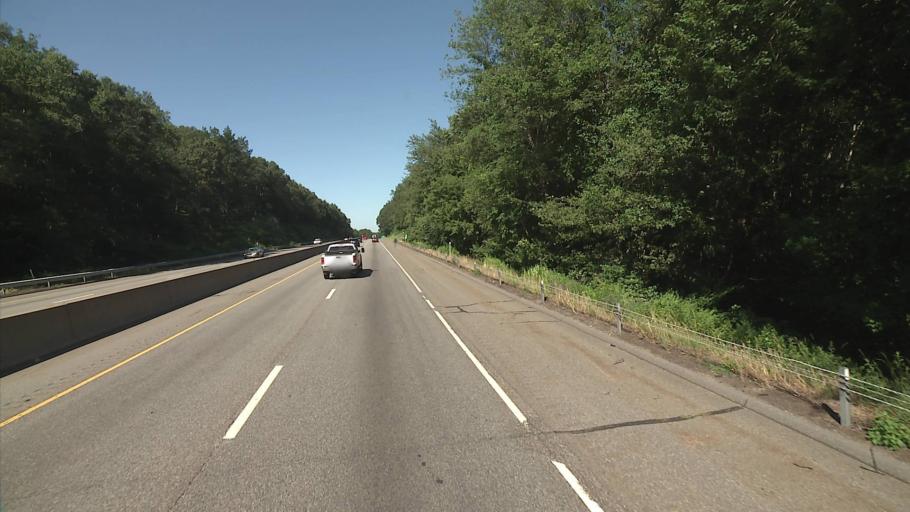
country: US
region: Connecticut
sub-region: Middlesex County
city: Saybrook Manor
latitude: 41.2938
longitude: -72.4076
